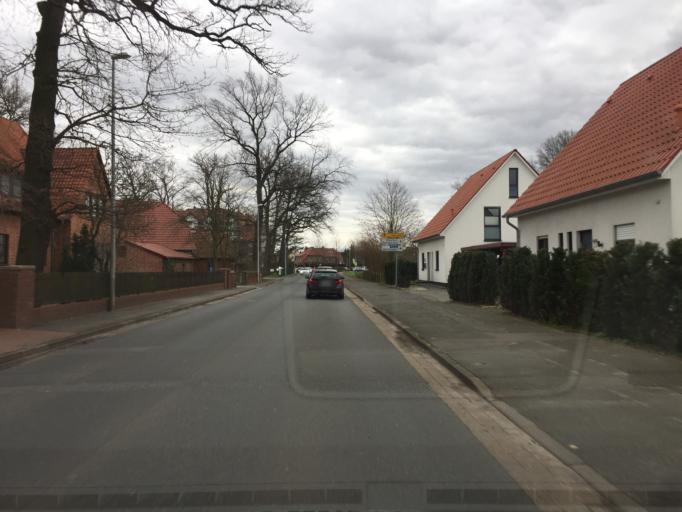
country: DE
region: Lower Saxony
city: Garbsen
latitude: 52.4404
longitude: 9.5711
